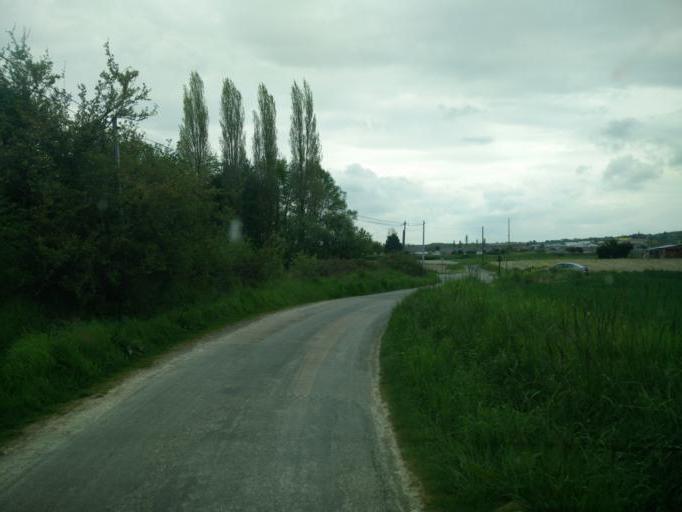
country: FR
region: Brittany
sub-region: Departement des Cotes-d'Armor
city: Yffiniac
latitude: 48.4947
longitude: -2.6753
